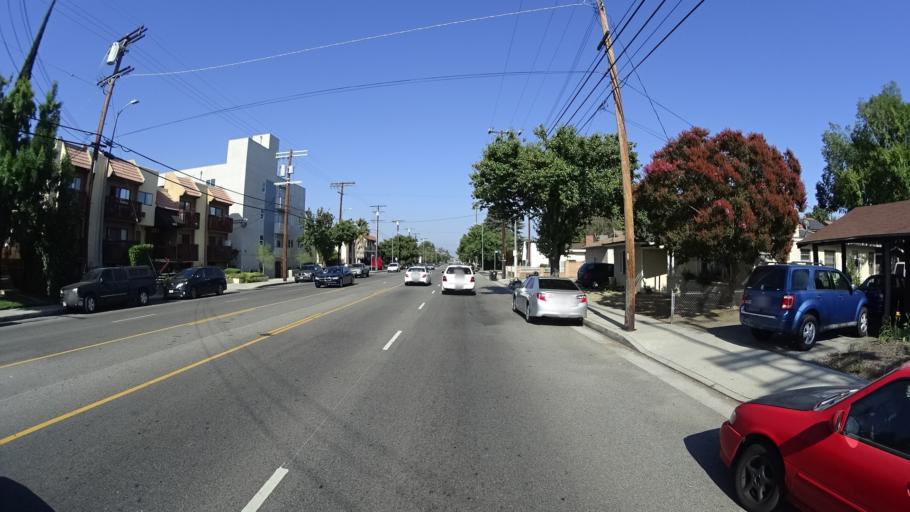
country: US
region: California
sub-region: Los Angeles County
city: North Hollywood
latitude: 34.1794
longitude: -118.4042
